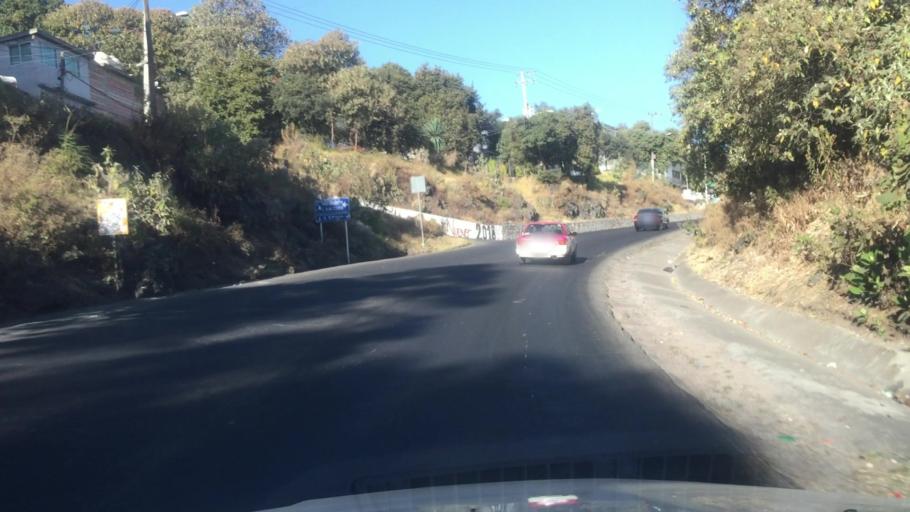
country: MX
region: Mexico City
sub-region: Tlalpan
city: Lomas de Tepemecatl
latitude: 19.2654
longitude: -99.2061
